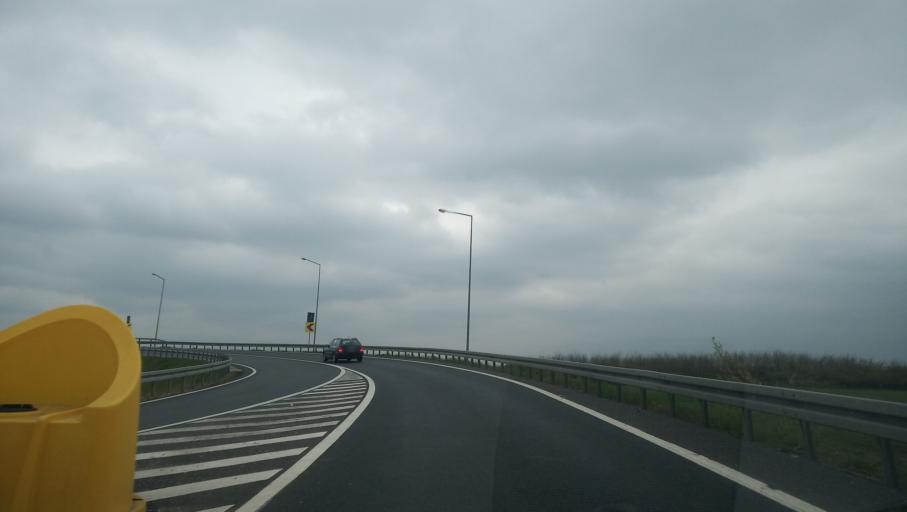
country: RO
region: Timis
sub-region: Comuna Remetea Mare
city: Remetea Mare
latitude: 45.8056
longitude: 21.4113
